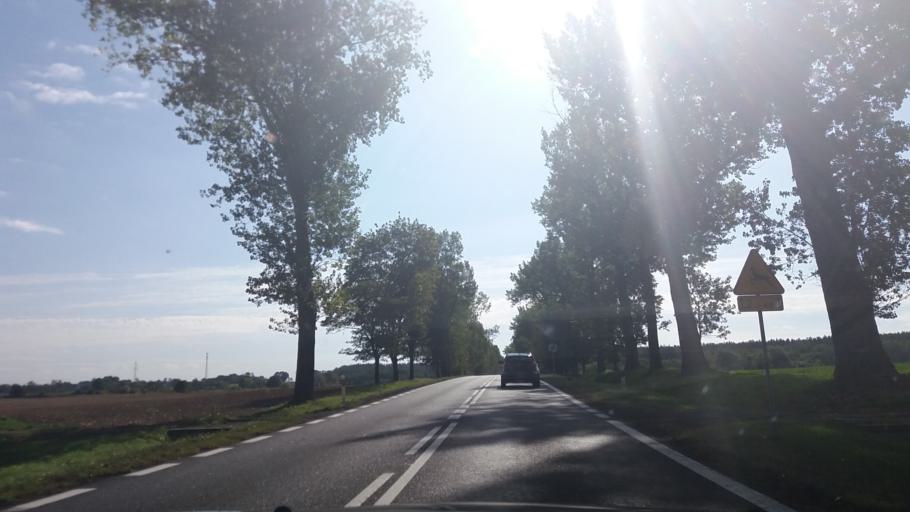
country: PL
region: Lower Silesian Voivodeship
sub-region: Powiat legnicki
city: Prochowice
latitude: 51.3127
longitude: 16.3273
